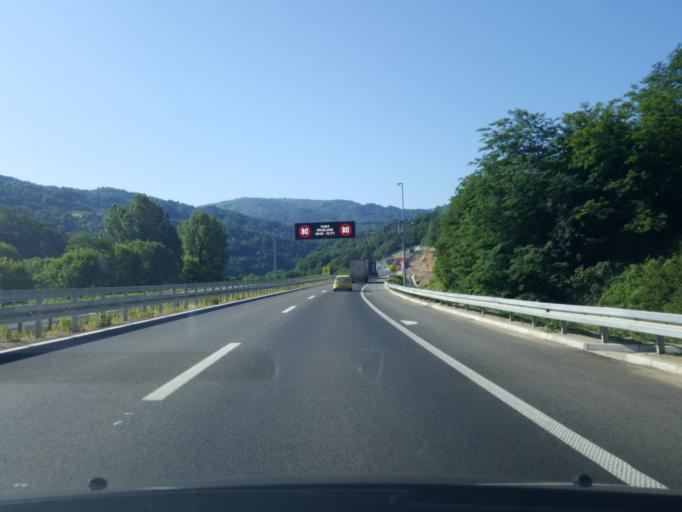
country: RS
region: Central Serbia
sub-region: Jablanicki Okrug
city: Vlasotince
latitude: 42.8501
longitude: 22.1285
